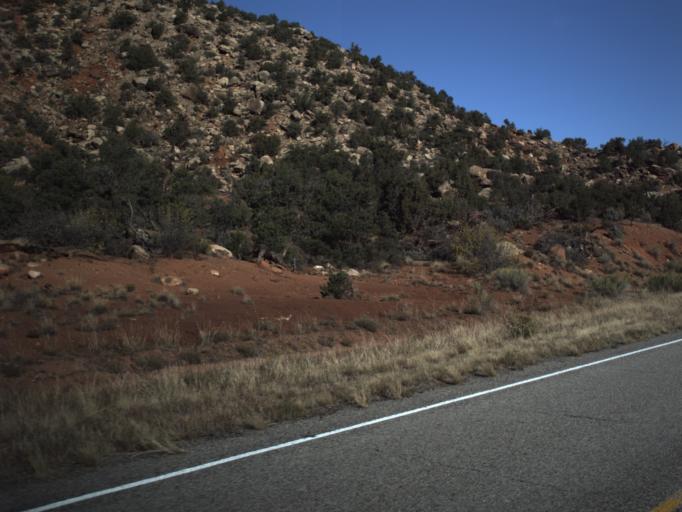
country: US
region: Utah
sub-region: San Juan County
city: Blanding
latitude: 37.5842
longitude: -110.0398
